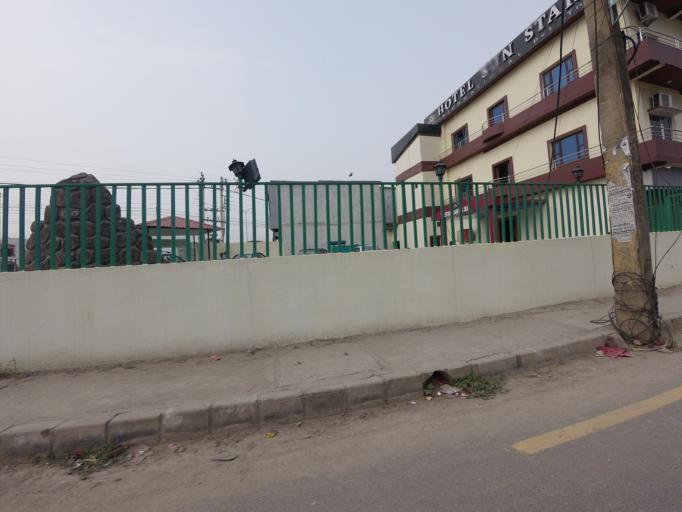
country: NP
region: Western Region
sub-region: Lumbini Zone
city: Bhairahawa
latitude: 27.5190
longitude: 83.4465
